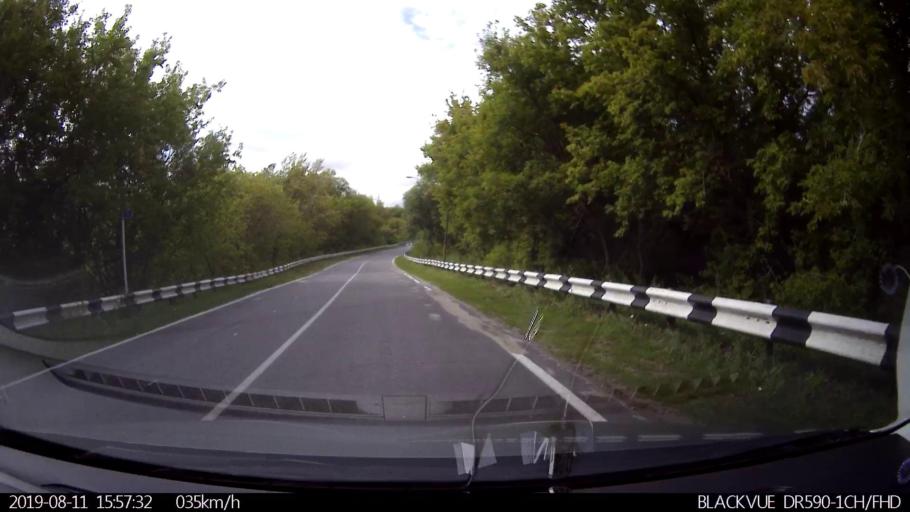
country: RU
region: Ulyanovsk
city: Ignatovka
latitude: 53.9514
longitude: 47.6522
